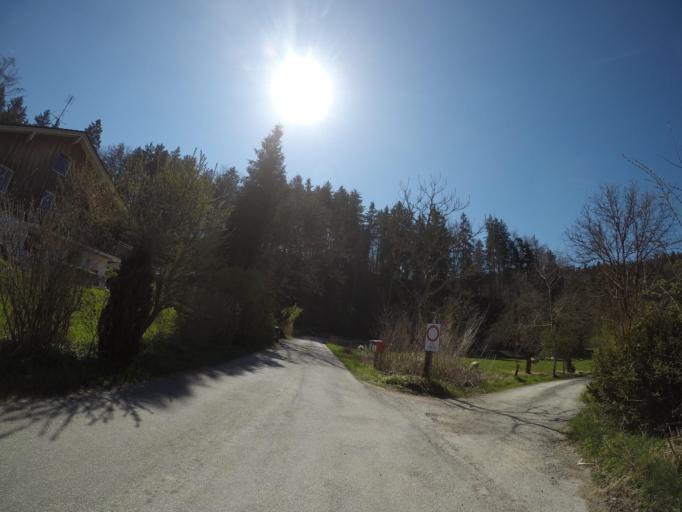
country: DE
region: Baden-Wuerttemberg
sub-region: Tuebingen Region
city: Horgenzell
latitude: 47.8174
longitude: 9.4640
